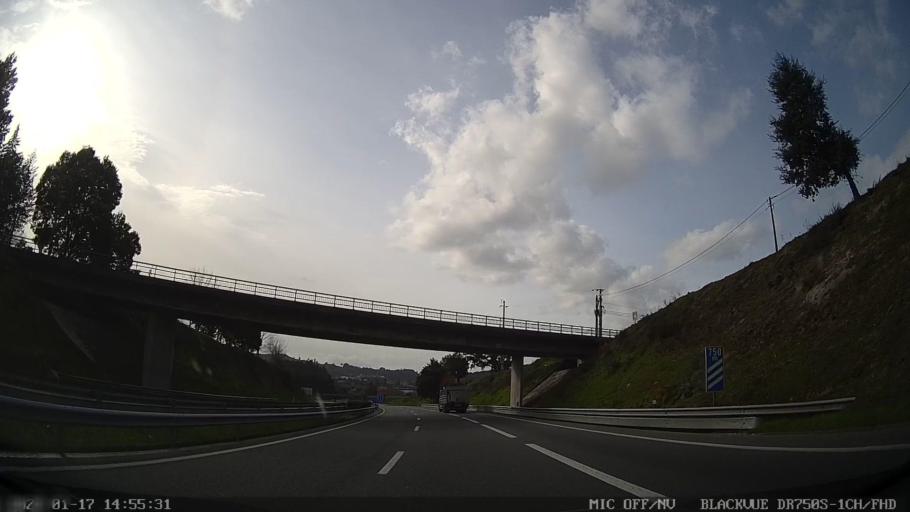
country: PT
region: Porto
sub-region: Lousada
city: Meinedo
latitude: 41.2374
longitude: -8.1925
